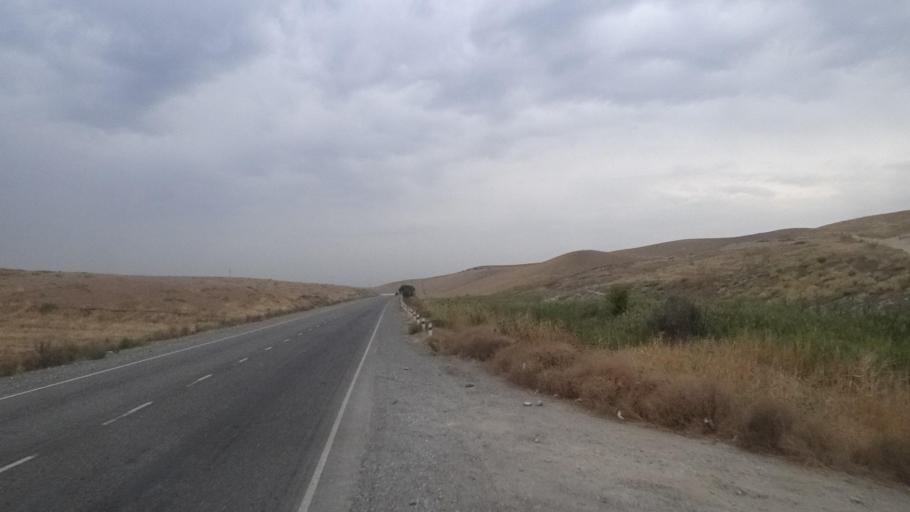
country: UZ
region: Namangan
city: Uchqurghon Shahri
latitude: 41.0544
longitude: 72.2366
